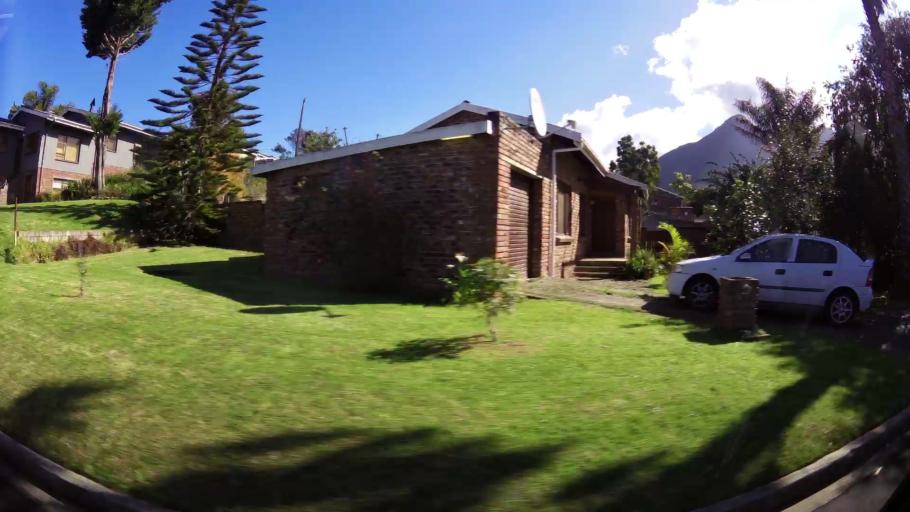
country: ZA
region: Western Cape
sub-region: Eden District Municipality
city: George
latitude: -33.9466
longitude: 22.4767
